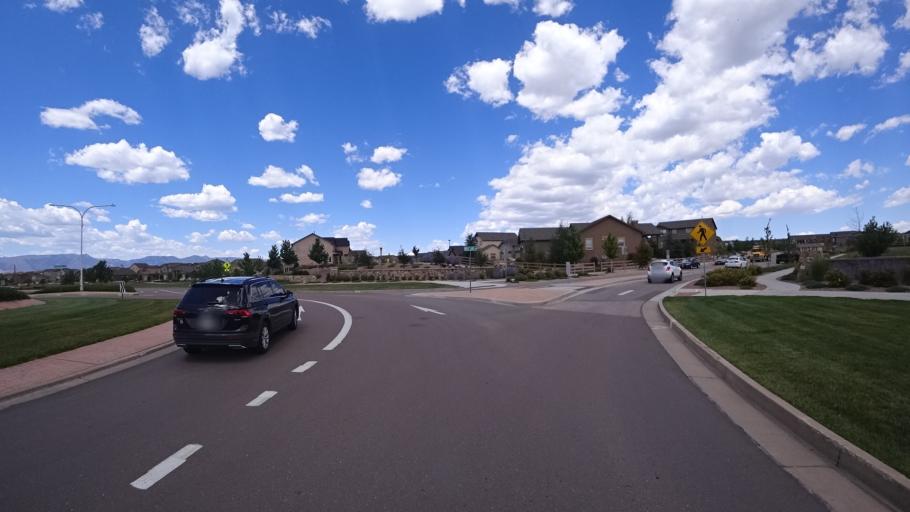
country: US
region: Colorado
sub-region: El Paso County
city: Black Forest
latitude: 38.9621
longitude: -104.7141
